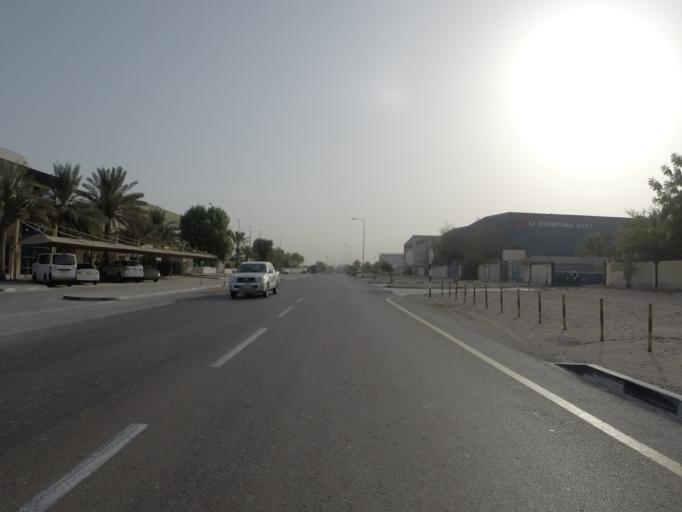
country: AE
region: Dubai
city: Dubai
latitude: 24.9705
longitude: 55.0719
